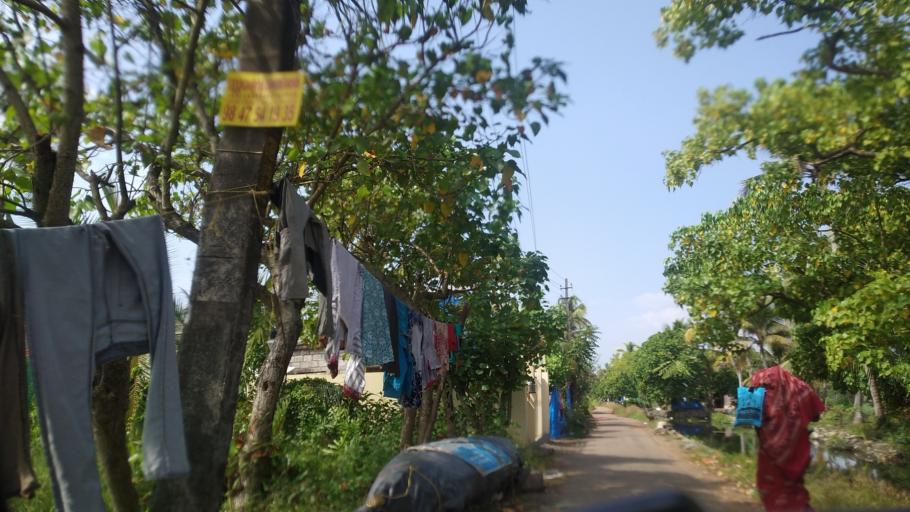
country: IN
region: Kerala
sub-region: Ernakulam
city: Elur
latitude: 10.0791
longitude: 76.2044
